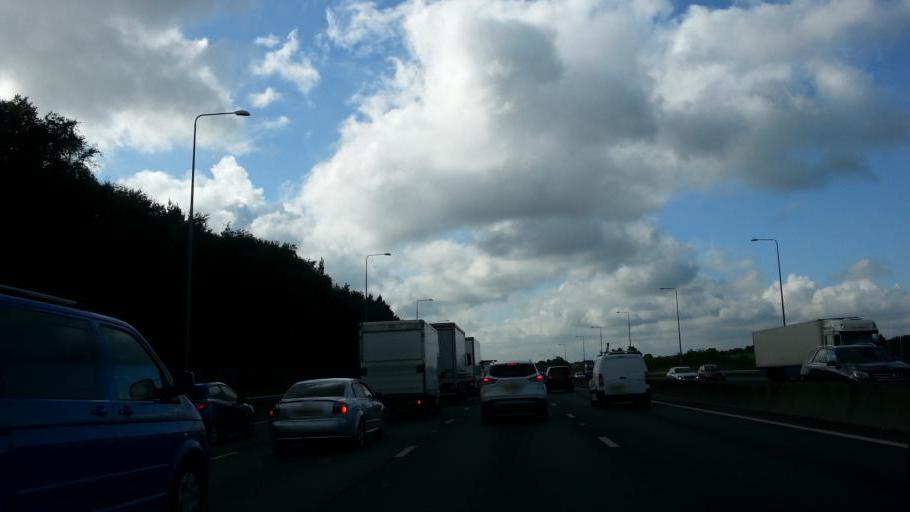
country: GB
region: England
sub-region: Buckinghamshire
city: Gerrards Cross
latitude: 51.5926
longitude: -0.5327
